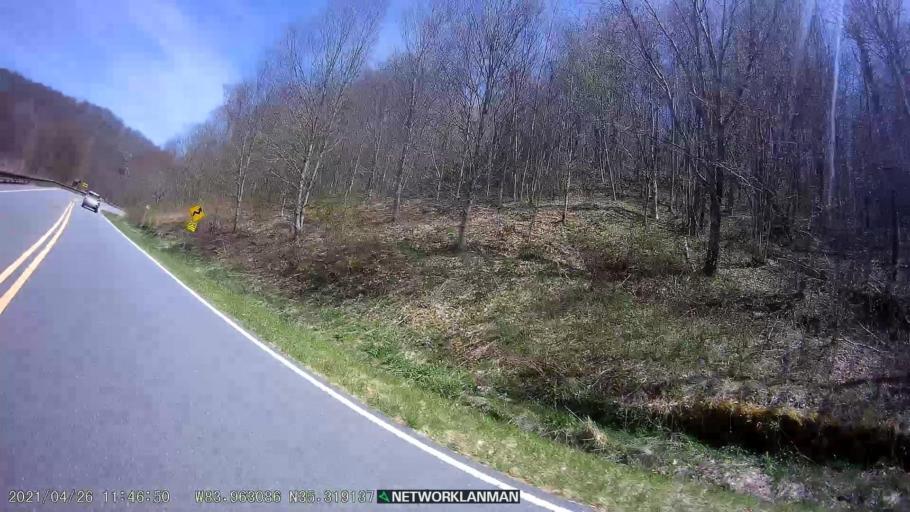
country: US
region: North Carolina
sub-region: Graham County
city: Robbinsville
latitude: 35.3192
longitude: -83.9630
